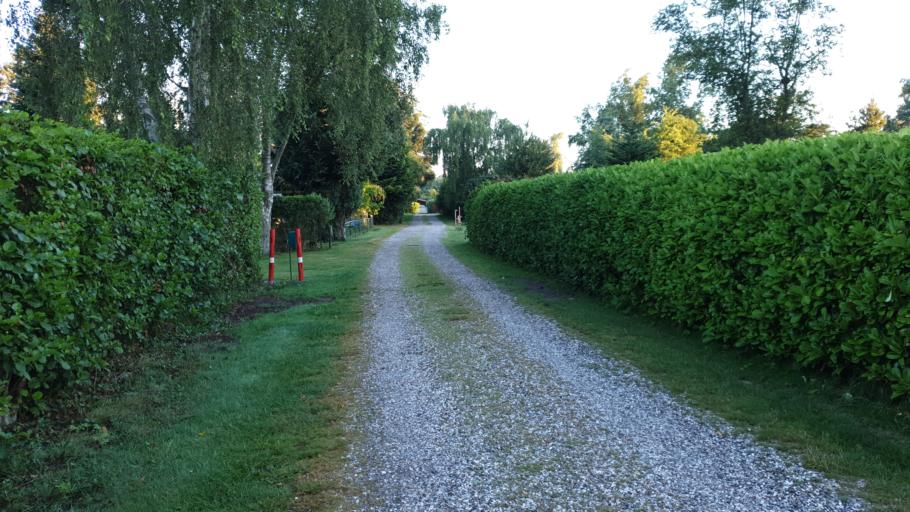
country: DK
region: Zealand
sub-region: Guldborgsund Kommune
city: Nykobing Falster
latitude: 54.7061
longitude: 11.9813
